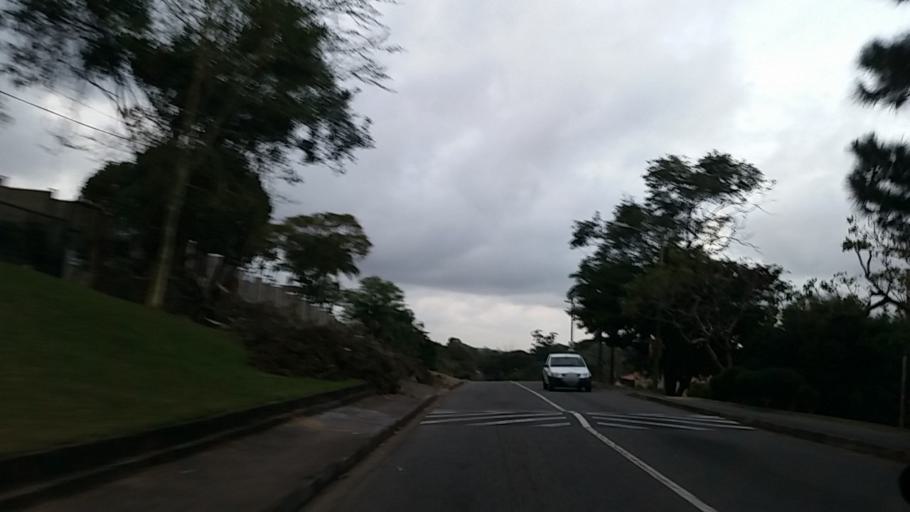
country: ZA
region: KwaZulu-Natal
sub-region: eThekwini Metropolitan Municipality
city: Berea
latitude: -29.8407
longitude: 30.9065
